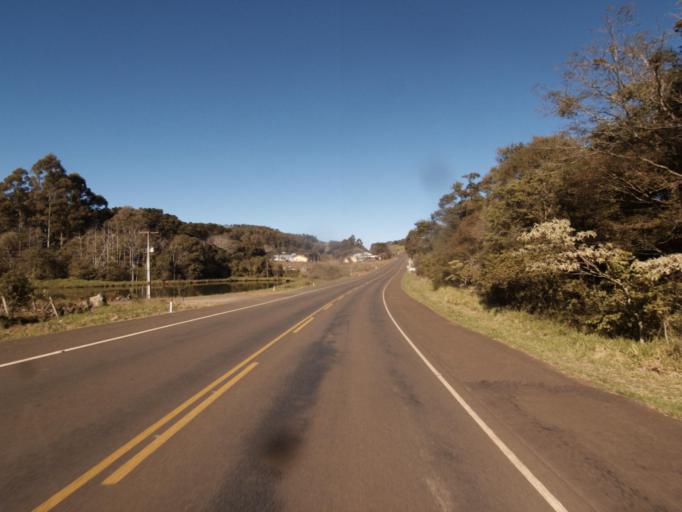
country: AR
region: Misiones
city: Bernardo de Irigoyen
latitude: -26.6759
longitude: -53.5635
